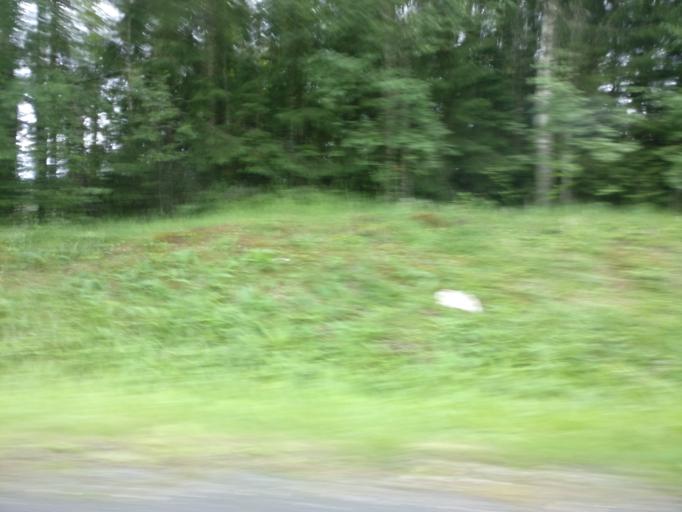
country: FI
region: Northern Savo
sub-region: Kuopio
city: Kuopio
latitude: 62.9834
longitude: 27.7870
